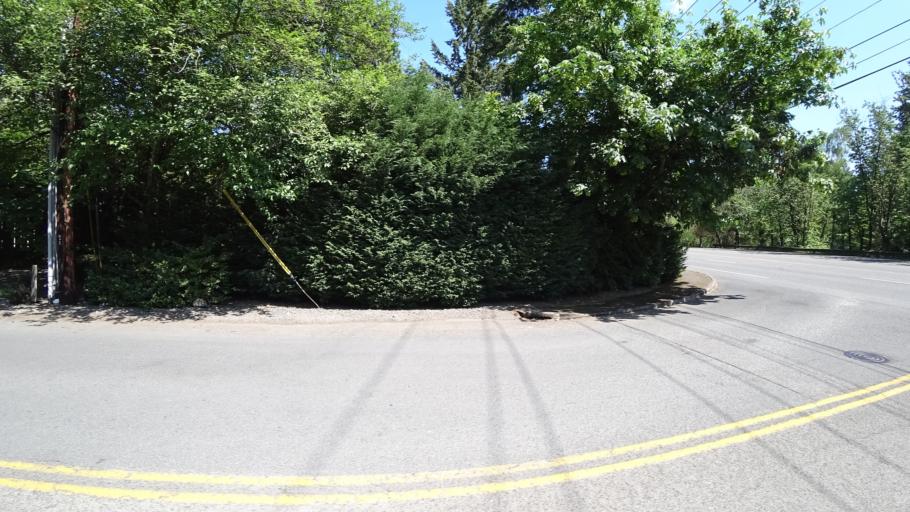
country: US
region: Oregon
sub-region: Clackamas County
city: Lake Oswego
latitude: 45.4233
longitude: -122.6949
